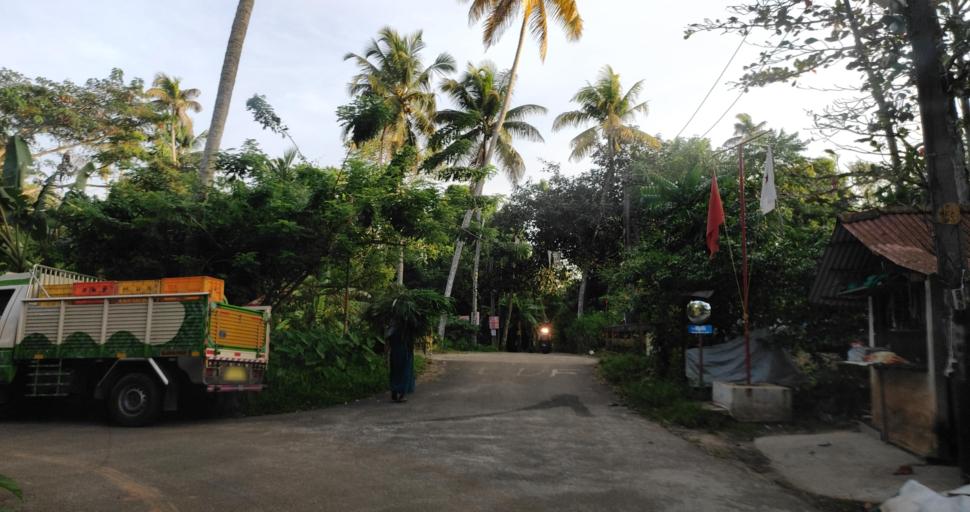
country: IN
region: Kerala
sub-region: Alappuzha
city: Shertallai
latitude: 9.6039
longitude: 76.3616
